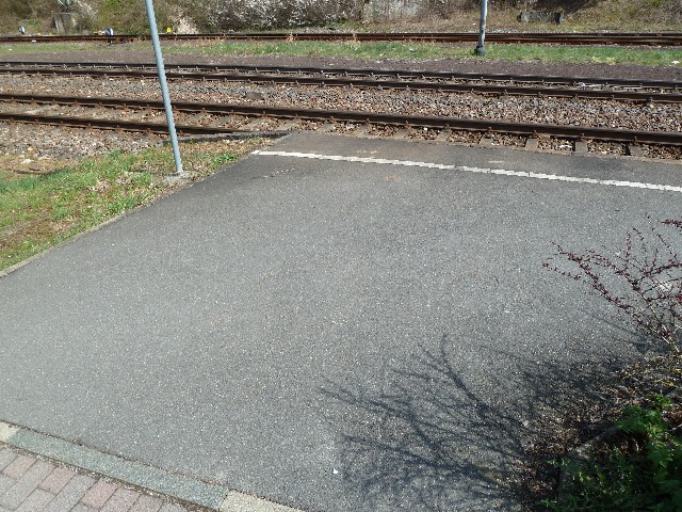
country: DE
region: Baden-Wuerttemberg
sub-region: Karlsruhe Region
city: Seckach
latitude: 49.4421
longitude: 9.3377
